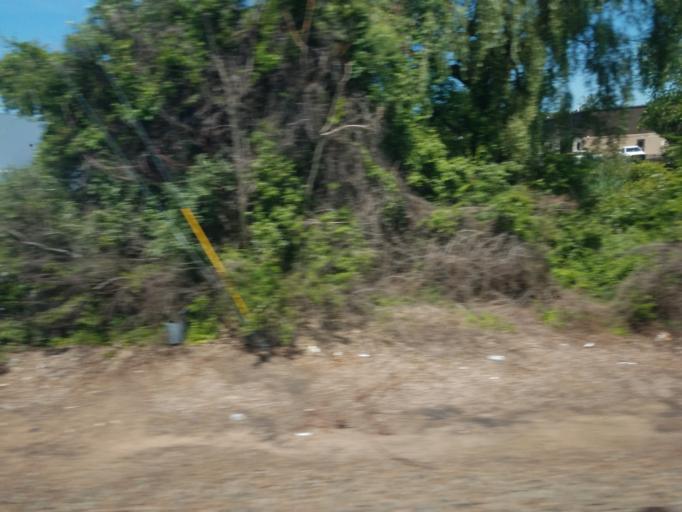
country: US
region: Connecticut
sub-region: New Haven County
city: North Haven
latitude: 41.3730
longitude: -72.8806
